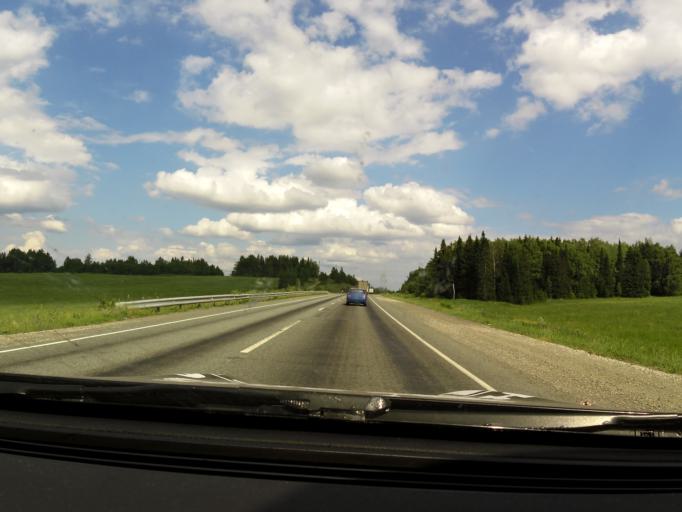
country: RU
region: Sverdlovsk
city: Bisert'
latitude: 56.8295
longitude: 59.0709
